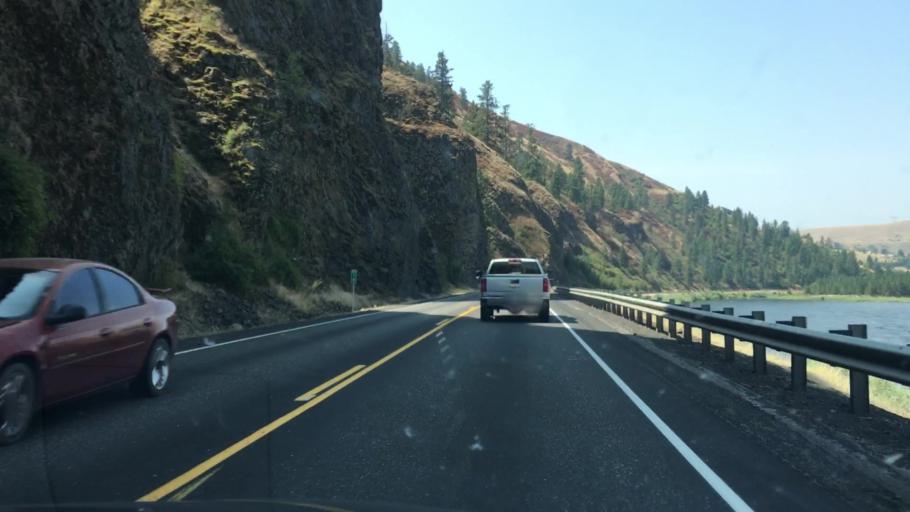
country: US
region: Idaho
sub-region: Nez Perce County
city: Lapwai
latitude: 46.4916
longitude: -116.7268
